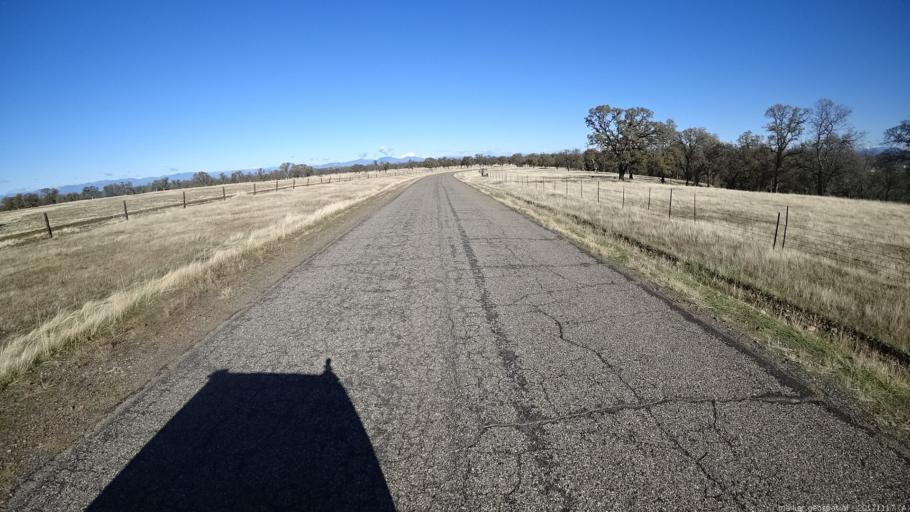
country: US
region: California
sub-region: Shasta County
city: Cottonwood
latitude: 40.4293
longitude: -122.1696
